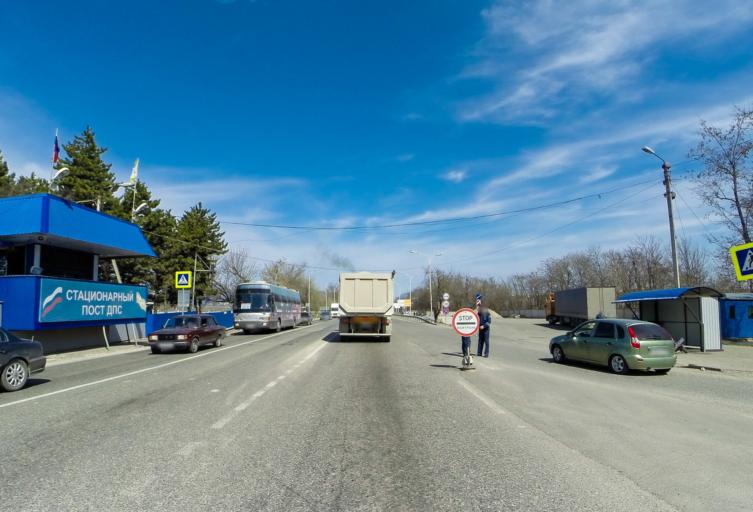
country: RU
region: Stavropol'skiy
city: Goryachevodskiy
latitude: 43.9802
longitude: 43.1326
